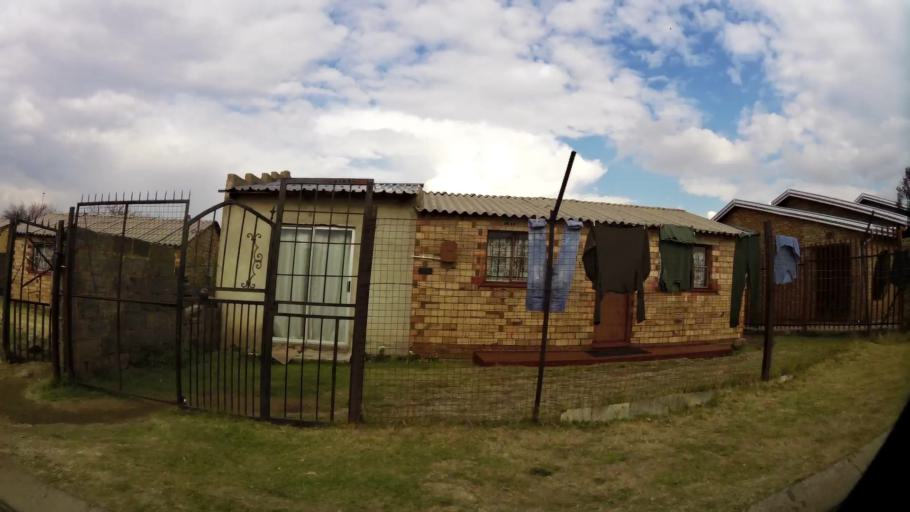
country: ZA
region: Gauteng
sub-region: City of Johannesburg Metropolitan Municipality
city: Soweto
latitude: -26.2388
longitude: 27.8618
